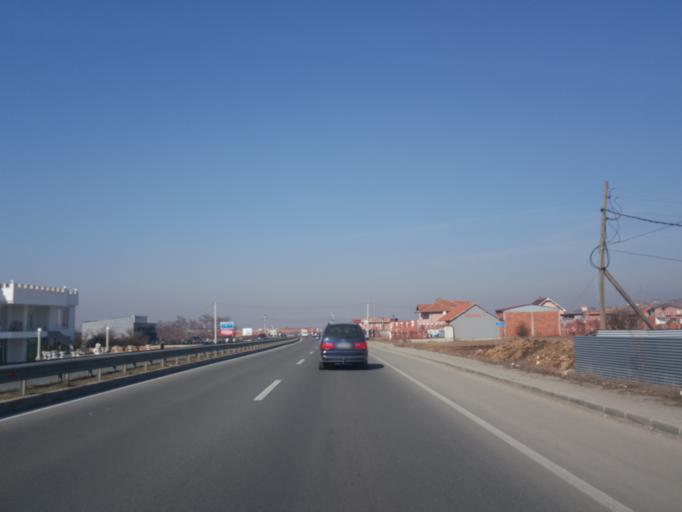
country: XK
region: Pristina
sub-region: Komuna e Obiliqit
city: Obiliq
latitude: 42.7482
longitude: 21.0444
